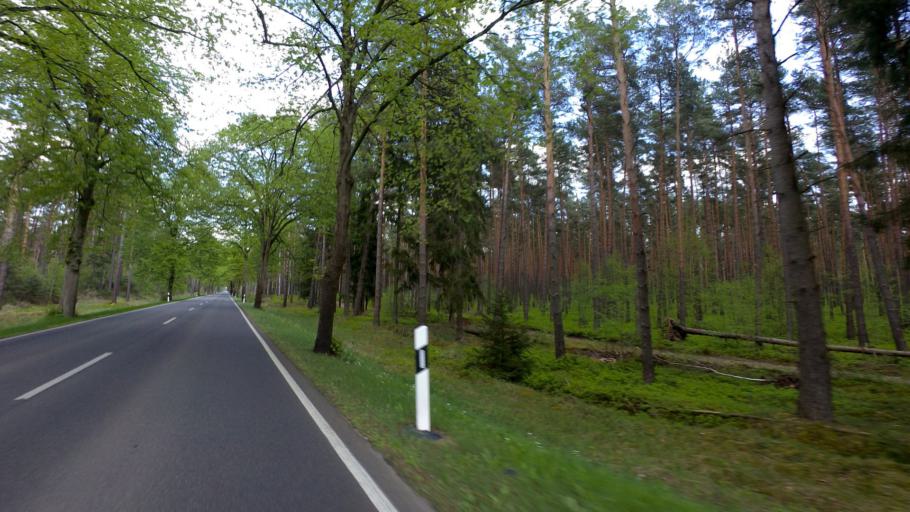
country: DE
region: Brandenburg
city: Marienwerder
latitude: 52.9497
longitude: 13.5621
